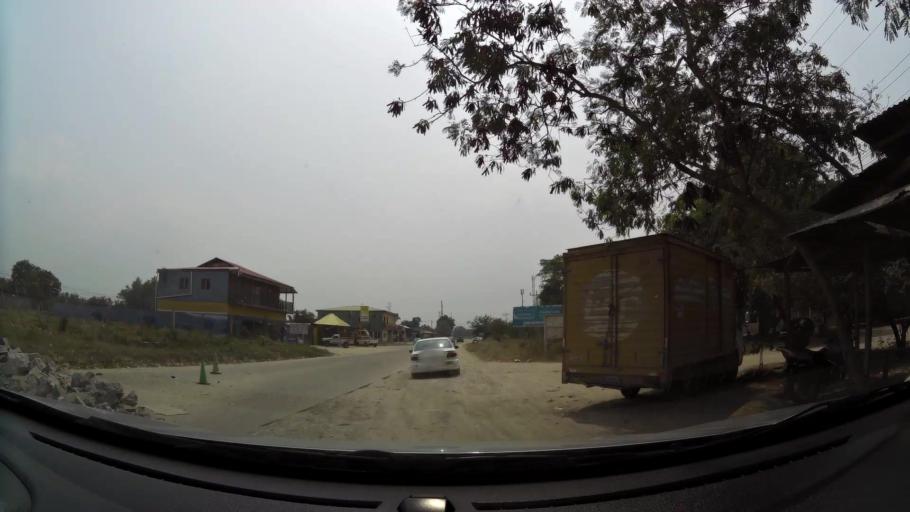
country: HN
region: Cortes
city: La Lima
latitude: 15.4367
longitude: -87.9056
